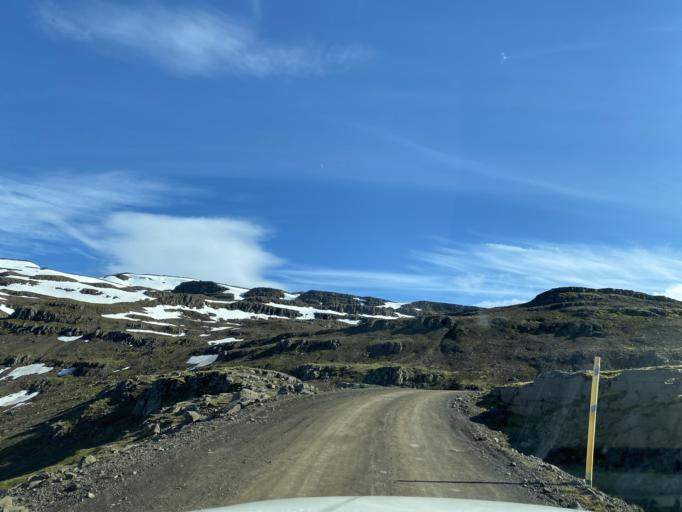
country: IS
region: East
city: Eskifjoerdur
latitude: 65.1683
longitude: -14.1288
